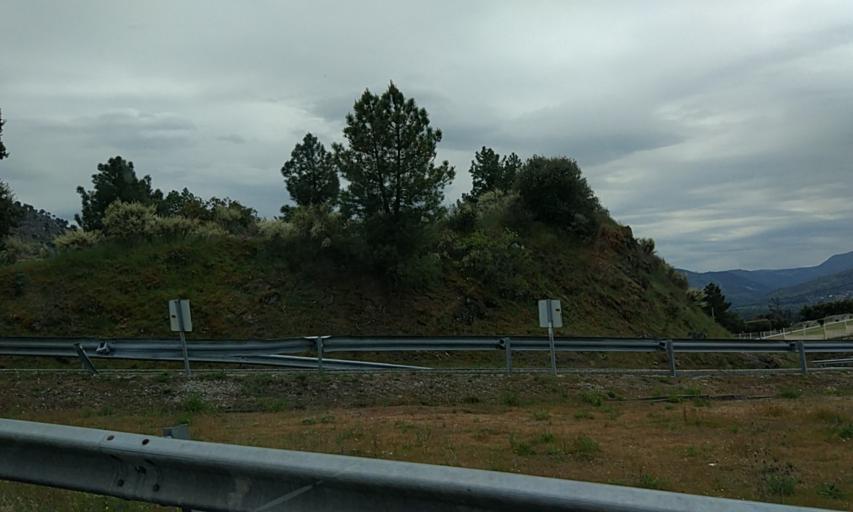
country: PT
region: Guarda
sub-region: Guarda
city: Guarda
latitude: 40.6191
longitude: -7.2867
